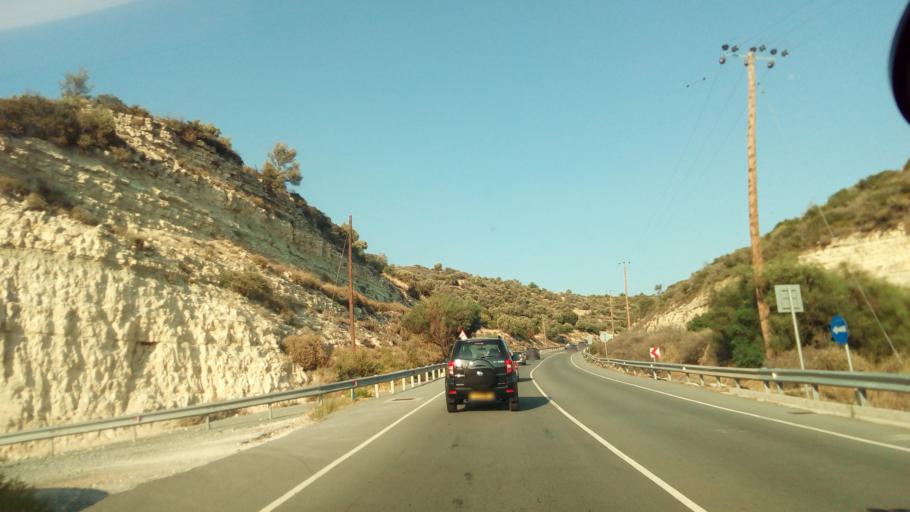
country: CY
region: Limassol
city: Pano Polemidia
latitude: 34.7692
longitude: 32.9389
